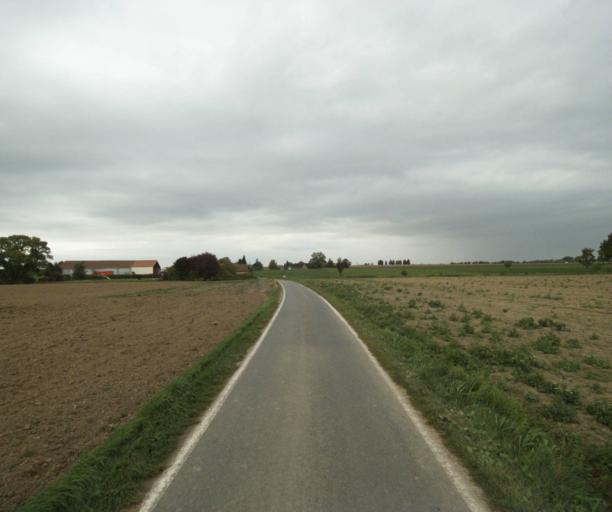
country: FR
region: Nord-Pas-de-Calais
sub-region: Departement du Nord
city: Marquillies
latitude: 50.5578
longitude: 2.8565
